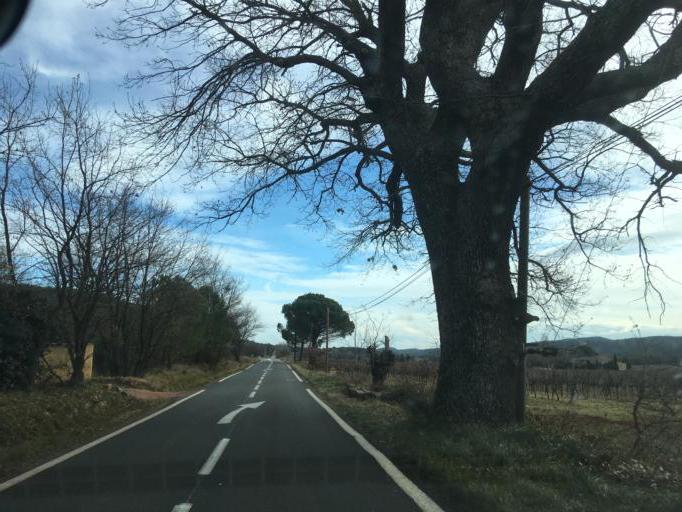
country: FR
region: Provence-Alpes-Cote d'Azur
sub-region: Departement du Var
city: Bras
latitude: 43.4470
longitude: 5.9995
